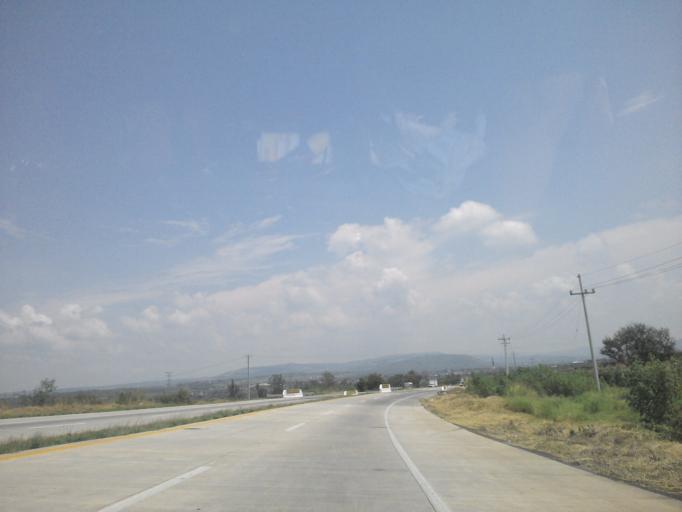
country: MX
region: Jalisco
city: Puente Grande
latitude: 20.5768
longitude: -103.1546
